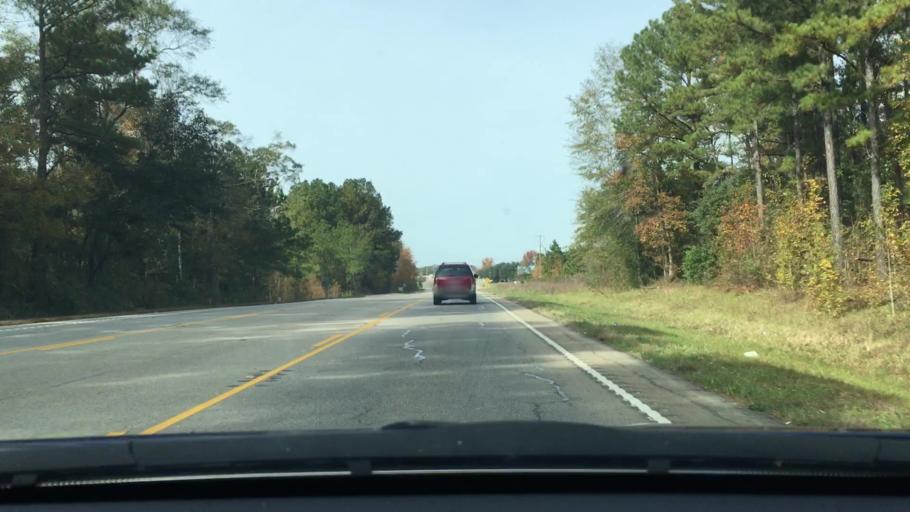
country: US
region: South Carolina
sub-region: Sumter County
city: Oakland
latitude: 33.9471
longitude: -80.4951
